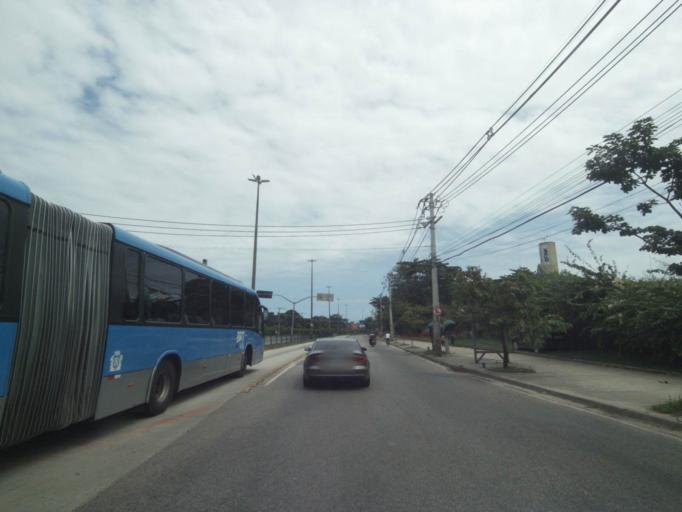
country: BR
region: Rio de Janeiro
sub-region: Sao Joao De Meriti
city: Sao Joao de Meriti
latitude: -22.9490
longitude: -43.3727
